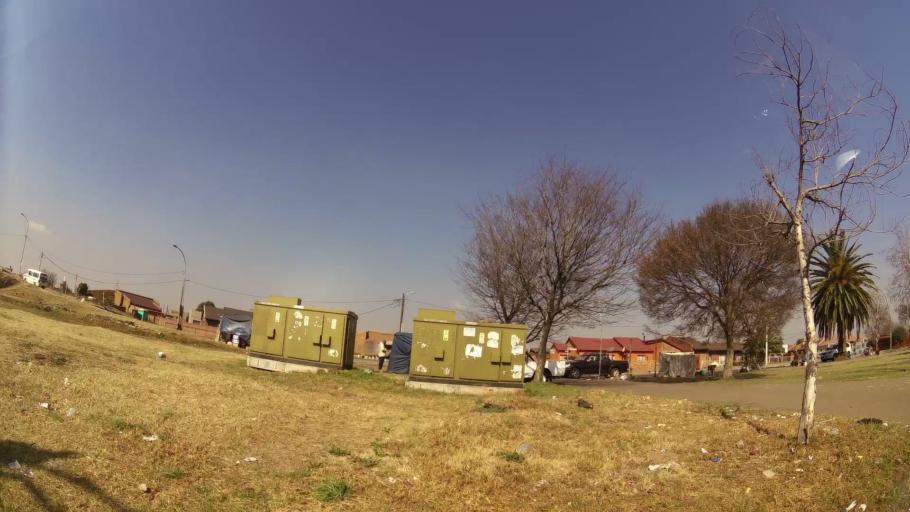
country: ZA
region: Gauteng
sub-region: Ekurhuleni Metropolitan Municipality
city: Boksburg
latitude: -26.2147
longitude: 28.2928
